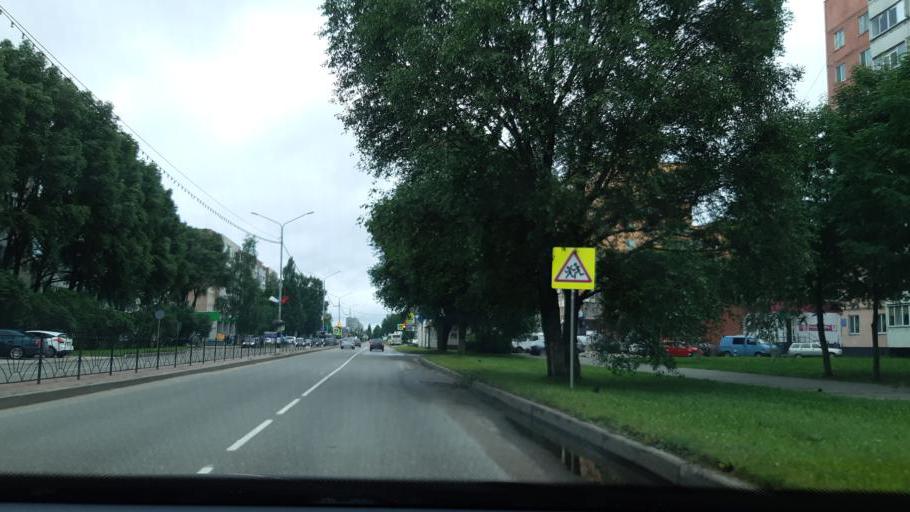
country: RU
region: Smolensk
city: Desnogorsk
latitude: 54.1482
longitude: 33.2842
